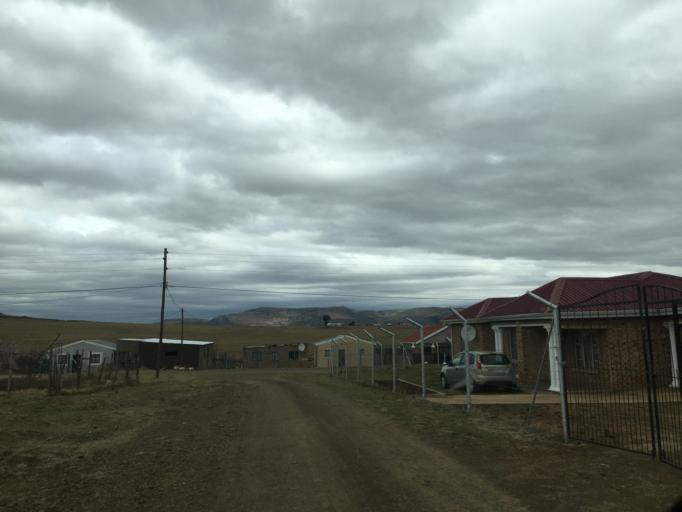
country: ZA
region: Eastern Cape
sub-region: Chris Hani District Municipality
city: Cala
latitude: -31.5401
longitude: 27.6955
